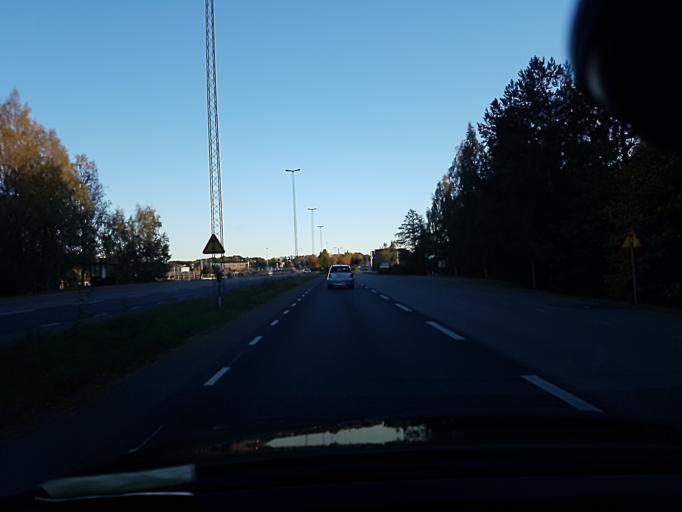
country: SE
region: Kronoberg
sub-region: Vaxjo Kommun
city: Vaexjoe
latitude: 56.8628
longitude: 14.8197
